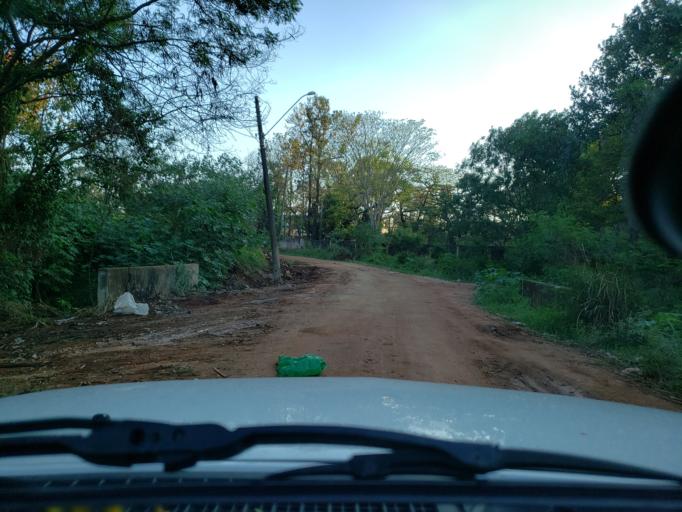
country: BR
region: Sao Paulo
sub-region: Moji-Guacu
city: Mogi-Gaucu
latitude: -22.3391
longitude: -46.9386
